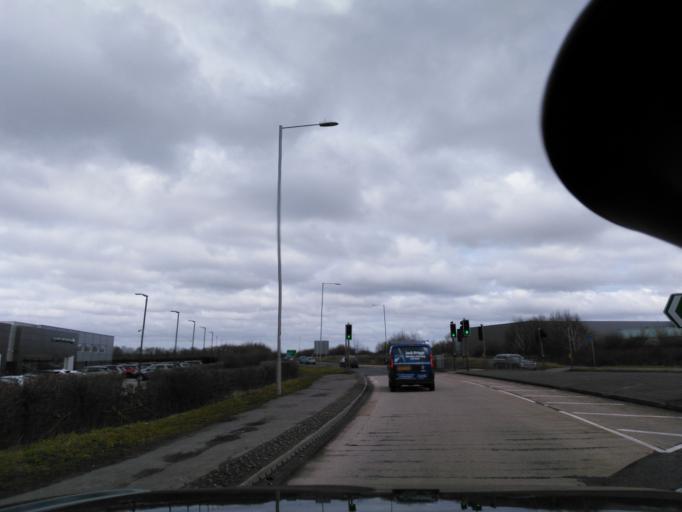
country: GB
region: England
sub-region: Wiltshire
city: Melksham
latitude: 51.3548
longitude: -2.1383
